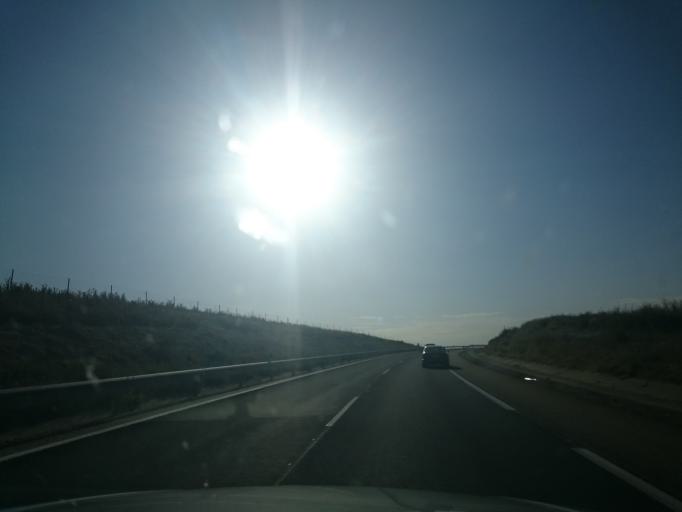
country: ES
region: Castille and Leon
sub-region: Provincia de Burgos
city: Villagonzalo-Pedernales
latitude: 42.3049
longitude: -3.7502
